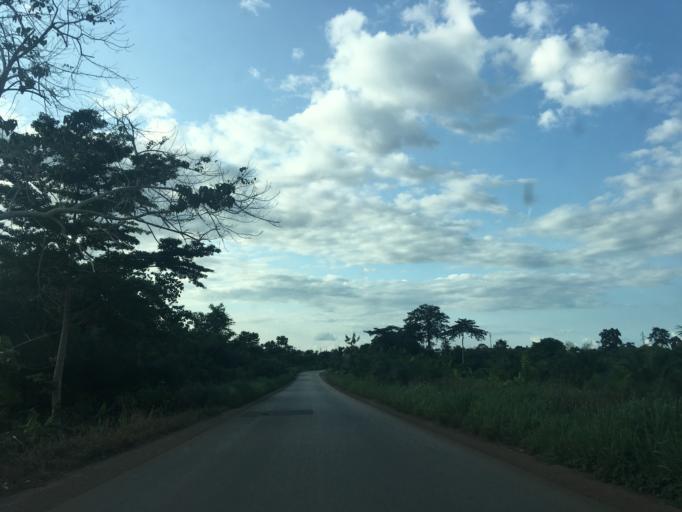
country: GH
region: Western
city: Bibiani
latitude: 6.3213
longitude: -2.2517
